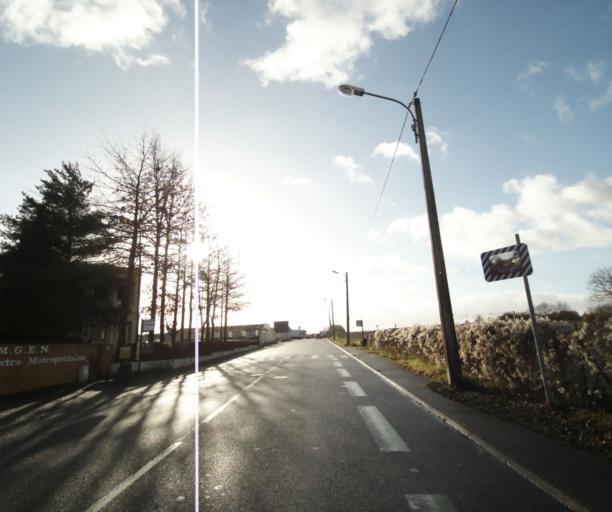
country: FR
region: Pays de la Loire
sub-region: Departement de la Sarthe
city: La Chapelle-Saint-Aubin
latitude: 48.0303
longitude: 0.1718
